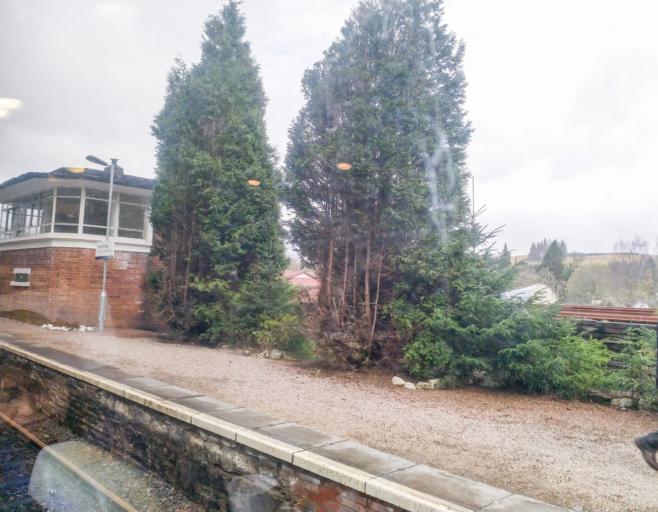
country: GB
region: Scotland
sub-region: Highland
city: Spean Bridge
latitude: 56.8901
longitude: -4.9204
